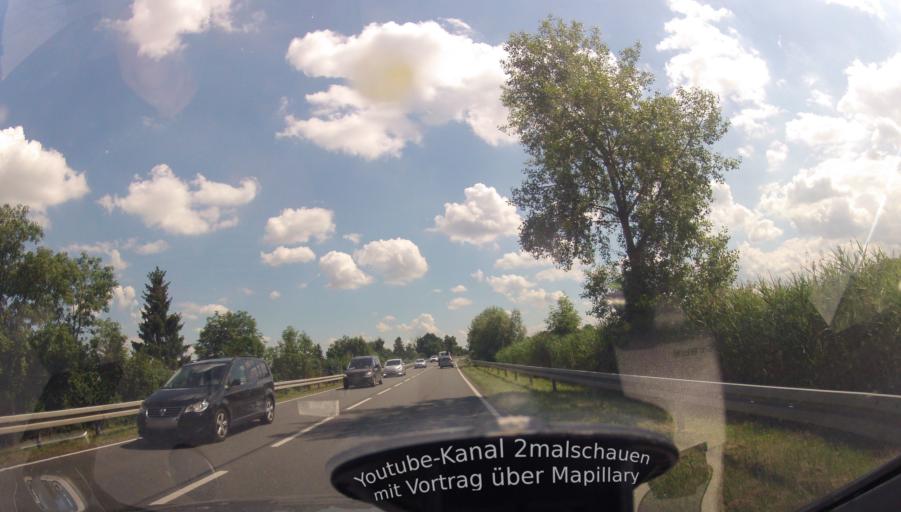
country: DE
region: Saxony
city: Torgau
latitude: 51.5393
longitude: 13.0028
